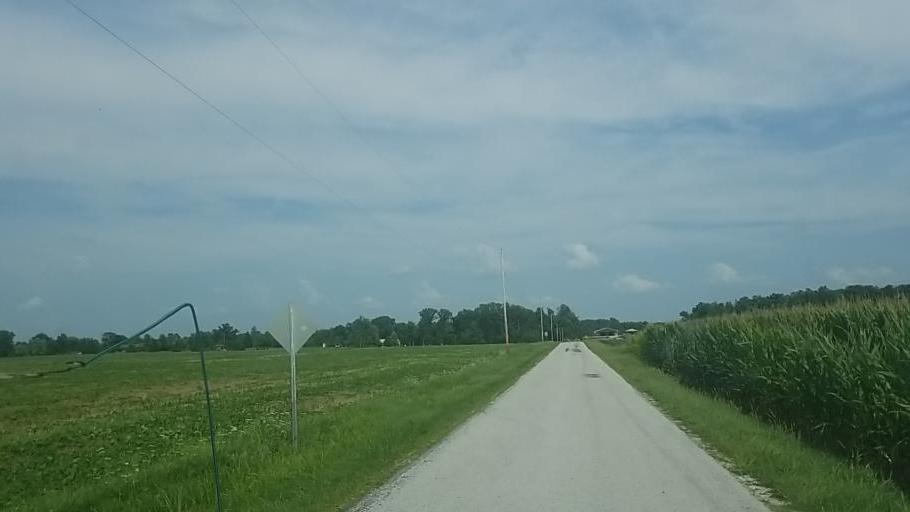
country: US
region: Ohio
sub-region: Hardin County
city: Forest
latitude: 40.7893
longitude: -83.5582
